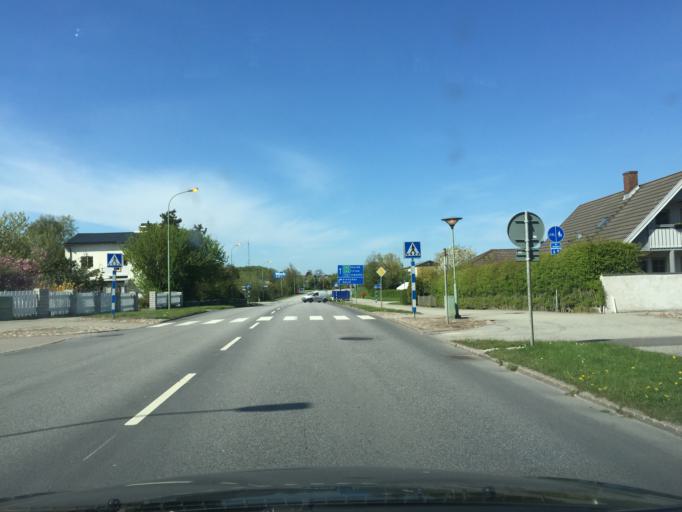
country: SE
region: Skane
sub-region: Skurups Kommun
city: Skurup
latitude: 55.4811
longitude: 13.5030
